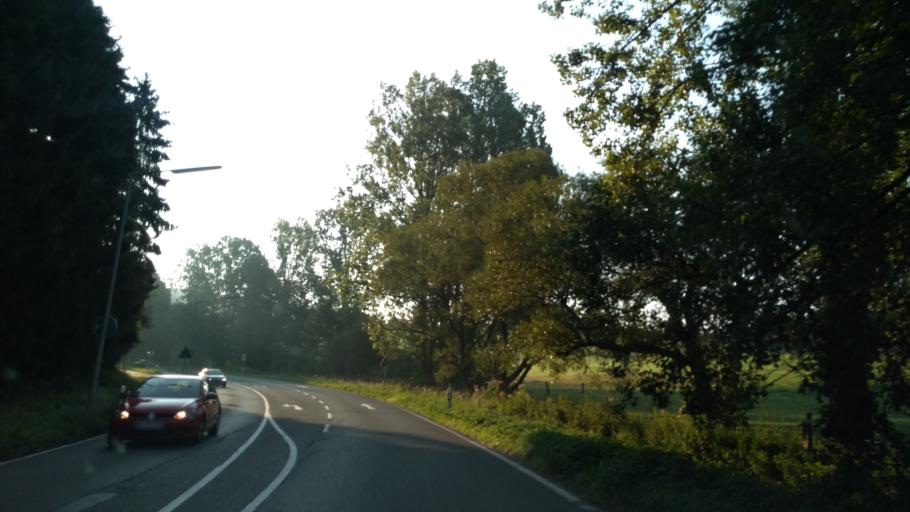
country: DE
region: North Rhine-Westphalia
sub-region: Regierungsbezirk Koln
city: Overath
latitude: 50.9354
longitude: 7.2965
